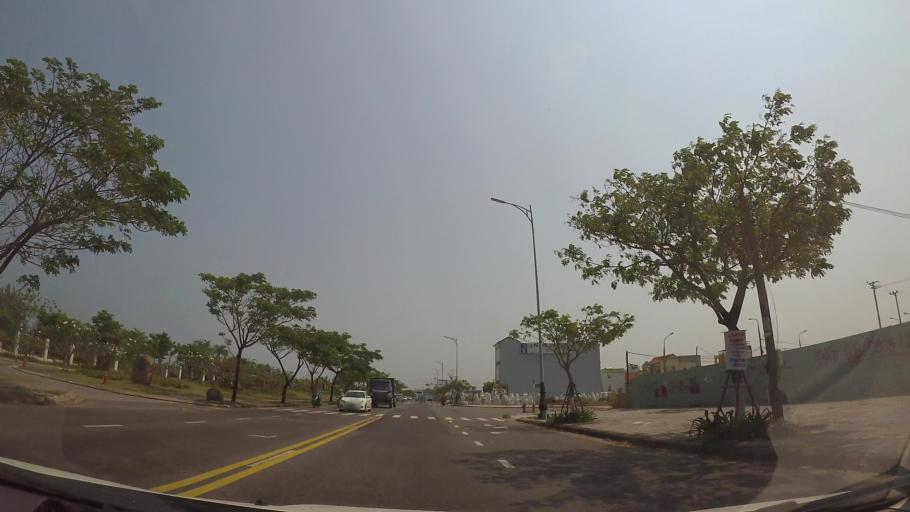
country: VN
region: Da Nang
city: Ngu Hanh Son
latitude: 15.9885
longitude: 108.2716
